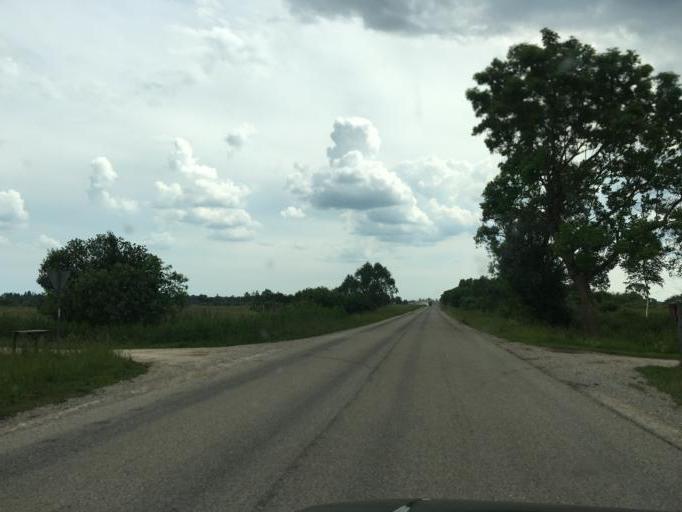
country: LV
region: Rugaju
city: Rugaji
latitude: 56.8942
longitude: 27.0690
